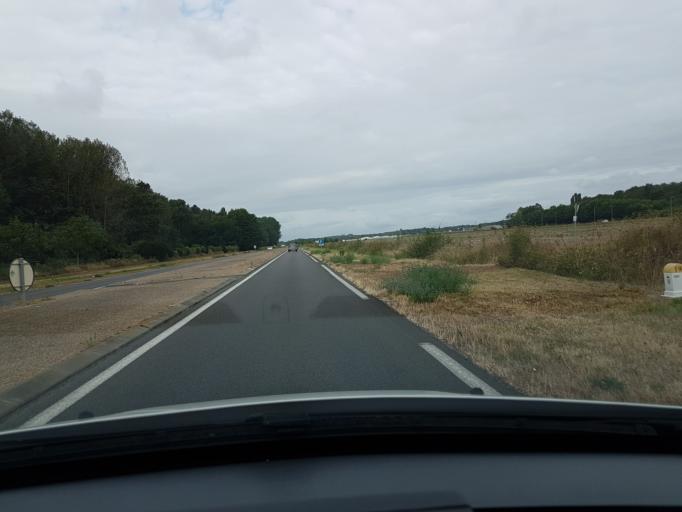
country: FR
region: Centre
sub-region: Departement d'Indre-et-Loire
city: Saint-Martin-le-Beau
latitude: 47.3572
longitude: 0.8906
